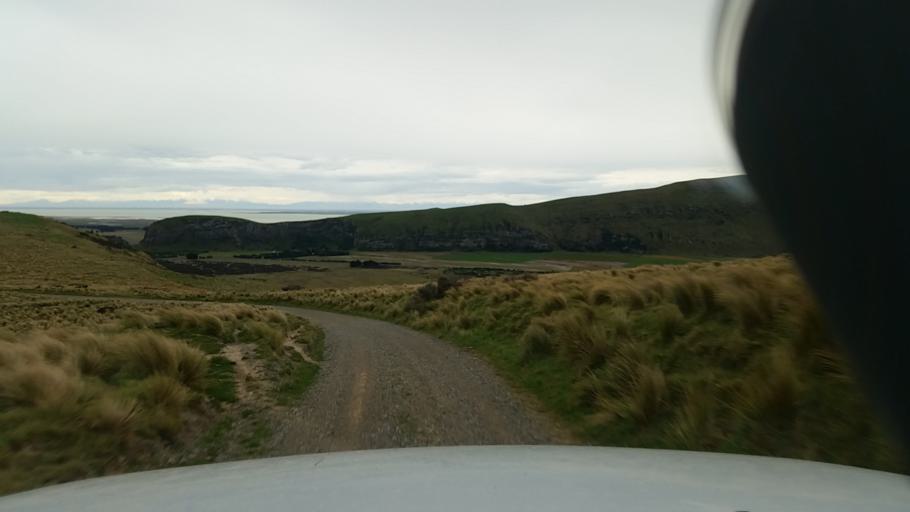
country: NZ
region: Canterbury
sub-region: Selwyn District
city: Lincoln
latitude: -43.8199
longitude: 172.7235
